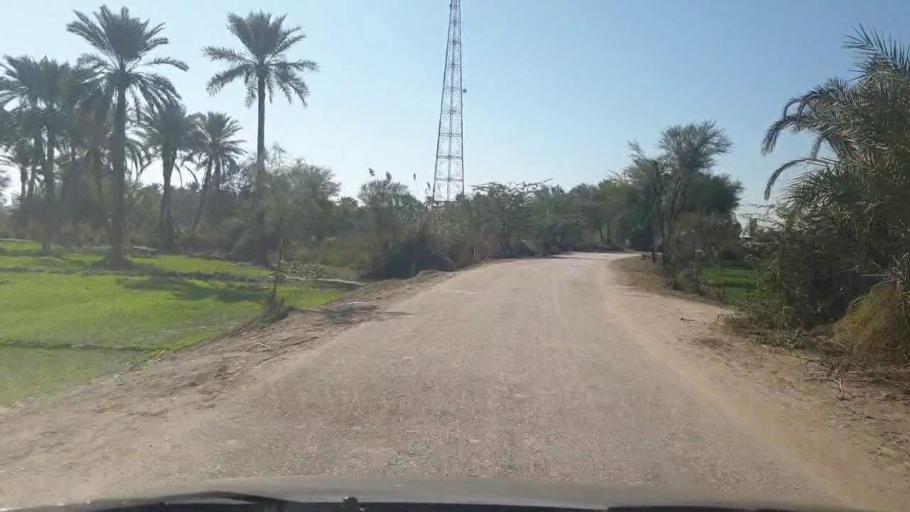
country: PK
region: Sindh
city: Bozdar
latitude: 27.1454
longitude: 68.6477
